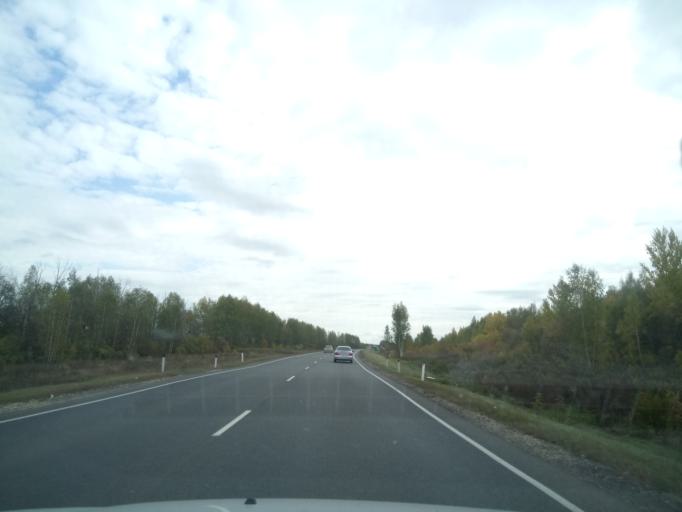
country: RU
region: Nizjnij Novgorod
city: Lukoyanov
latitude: 55.0613
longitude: 44.3599
